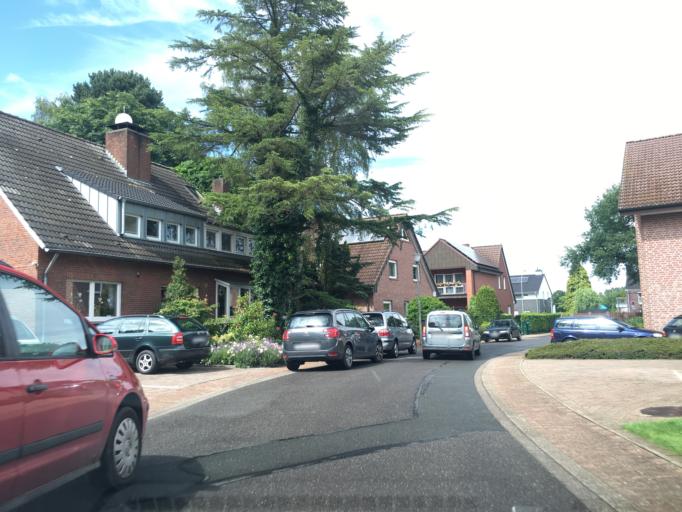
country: DE
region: North Rhine-Westphalia
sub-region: Regierungsbezirk Munster
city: Greven
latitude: 52.0385
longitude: 7.6147
